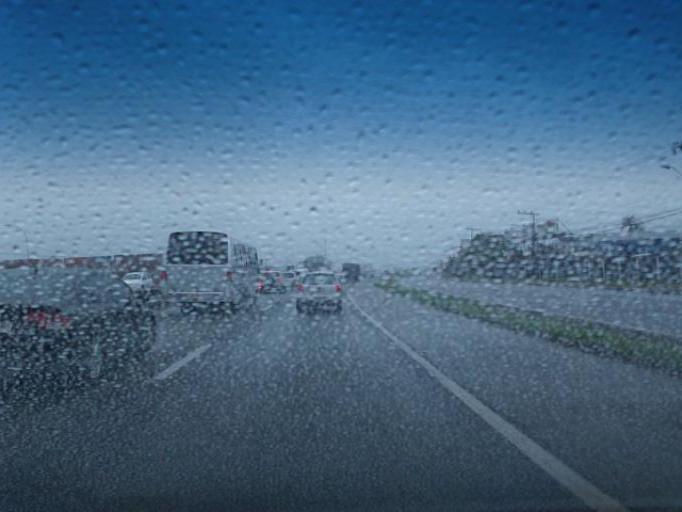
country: BR
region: Santa Catarina
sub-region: Itajai
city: Itajai
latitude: -26.8667
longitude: -48.7300
